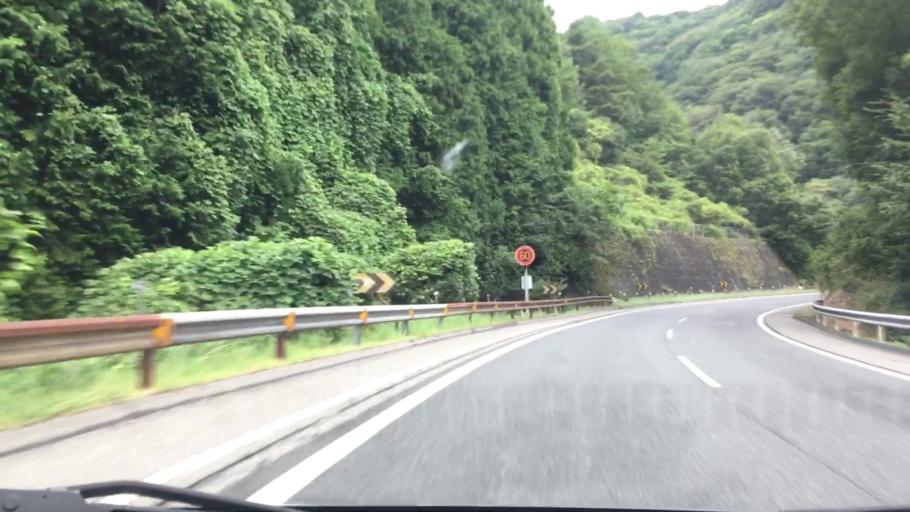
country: JP
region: Okayama
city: Niimi
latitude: 34.9875
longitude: 133.6061
